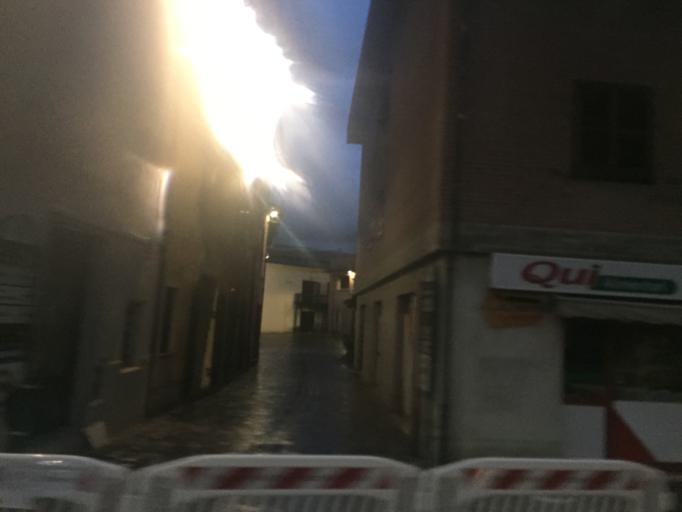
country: IT
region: The Marches
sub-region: Provincia di Macerata
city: Muccia
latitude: 43.0821
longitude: 13.0435
